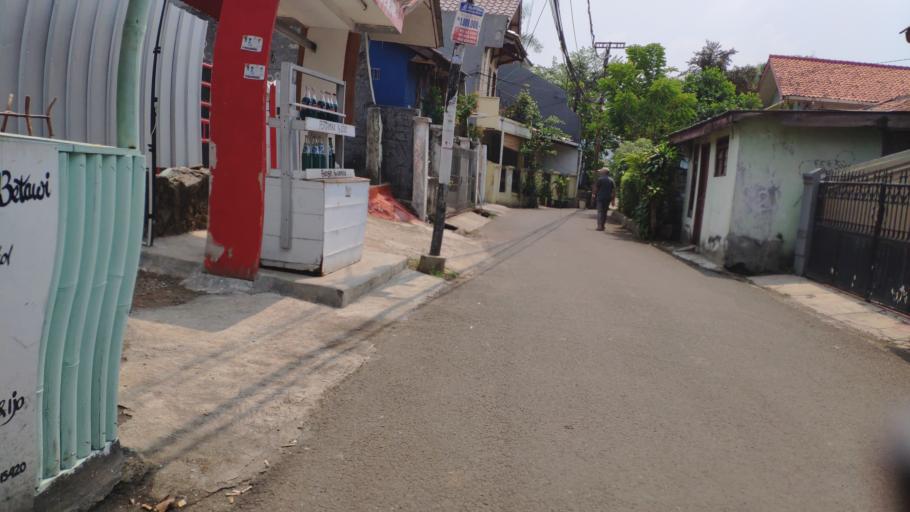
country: ID
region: West Java
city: Pamulang
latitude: -6.3039
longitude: 106.8185
